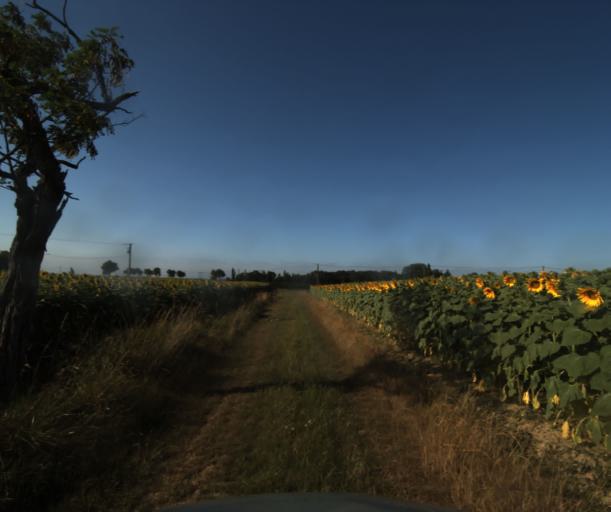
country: FR
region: Midi-Pyrenees
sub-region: Departement de la Haute-Garonne
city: Labarthe-sur-Leze
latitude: 43.4449
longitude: 1.3808
